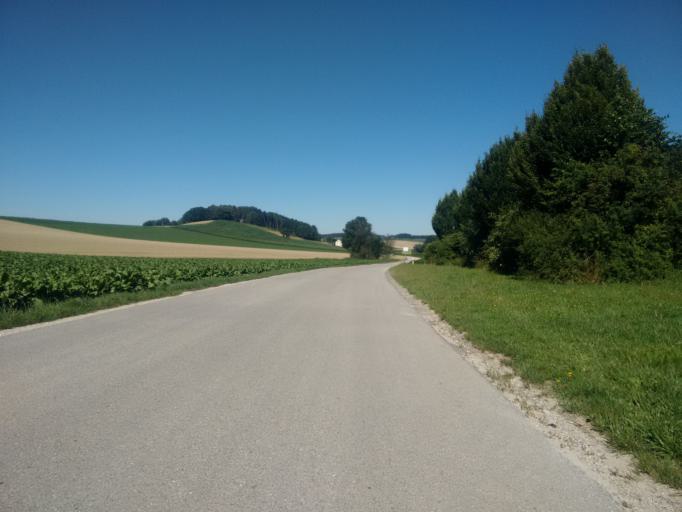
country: AT
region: Upper Austria
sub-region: Wels-Land
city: Buchkirchen
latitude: 48.2203
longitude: 13.9935
